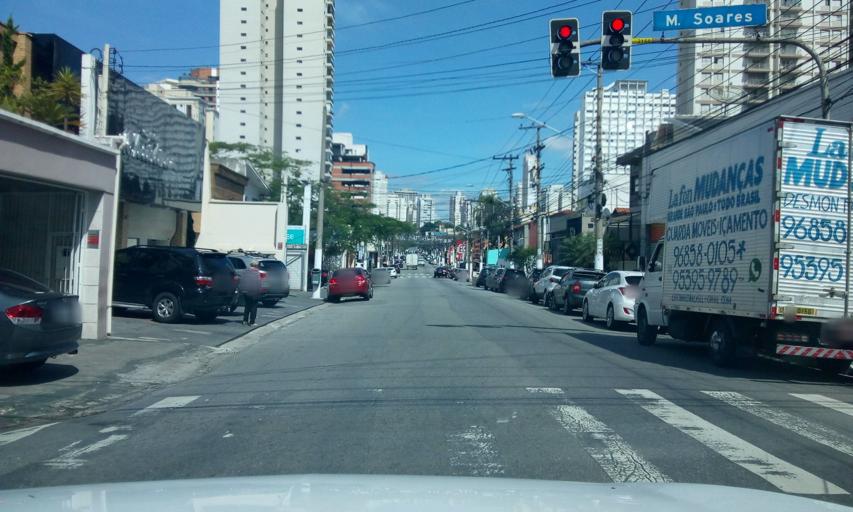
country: BR
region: Sao Paulo
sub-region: Sao Paulo
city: Sao Paulo
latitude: -23.6206
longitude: -46.6737
